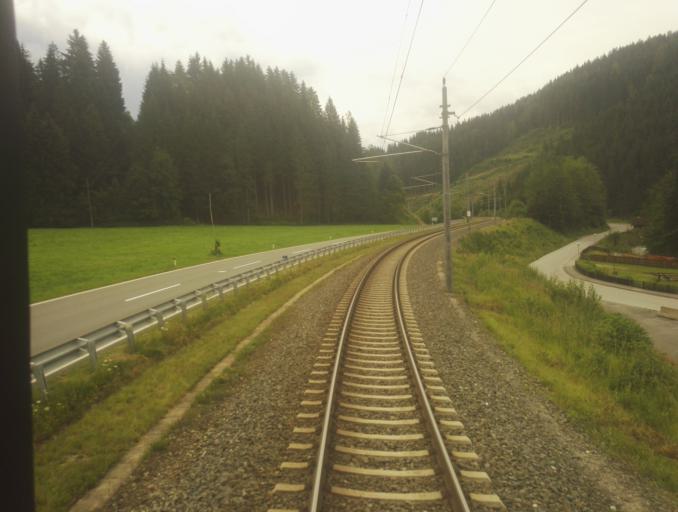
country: AT
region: Salzburg
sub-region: Politischer Bezirk Sankt Johann im Pongau
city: Huttau
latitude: 47.4226
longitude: 13.3386
